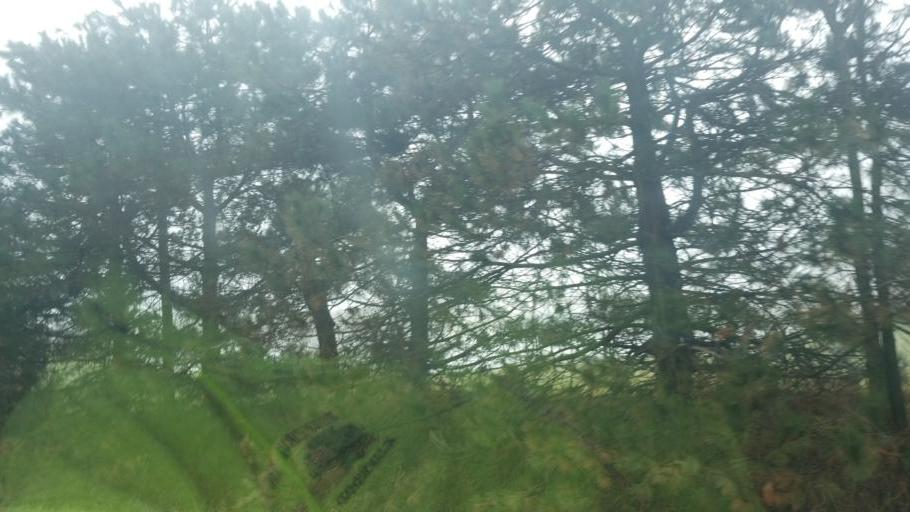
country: US
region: Ohio
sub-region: Champaign County
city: North Lewisburg
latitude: 40.3095
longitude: -83.6189
